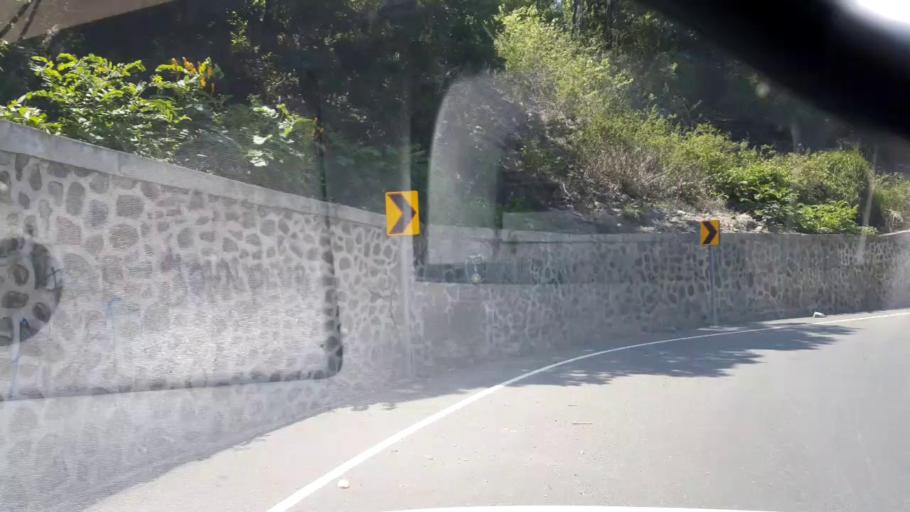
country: TL
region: Liquica
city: Maubara
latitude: -8.6607
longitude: 125.1151
